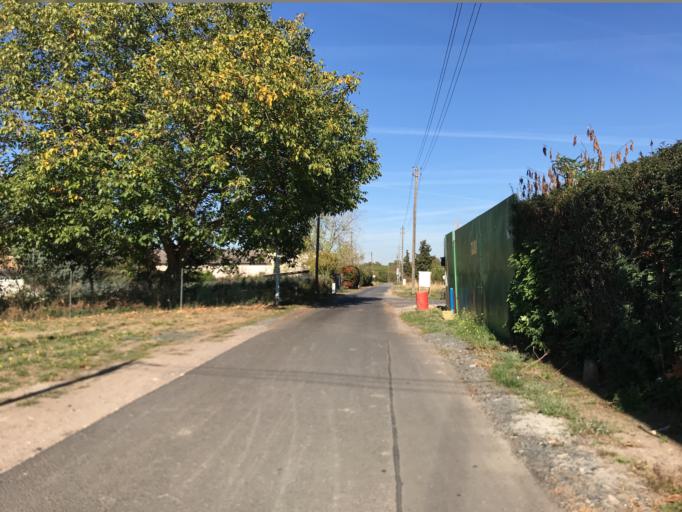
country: DE
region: Rheinland-Pfalz
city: Mainz
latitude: 50.0103
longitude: 8.3101
